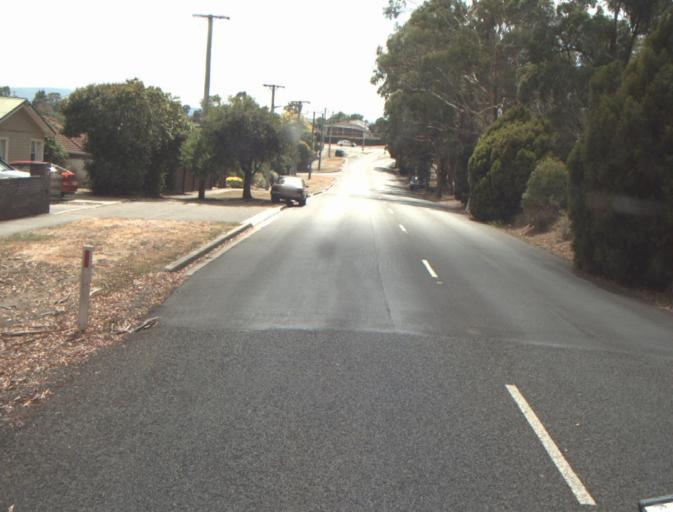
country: AU
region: Tasmania
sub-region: Launceston
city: Newstead
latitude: -41.4648
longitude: 147.1712
